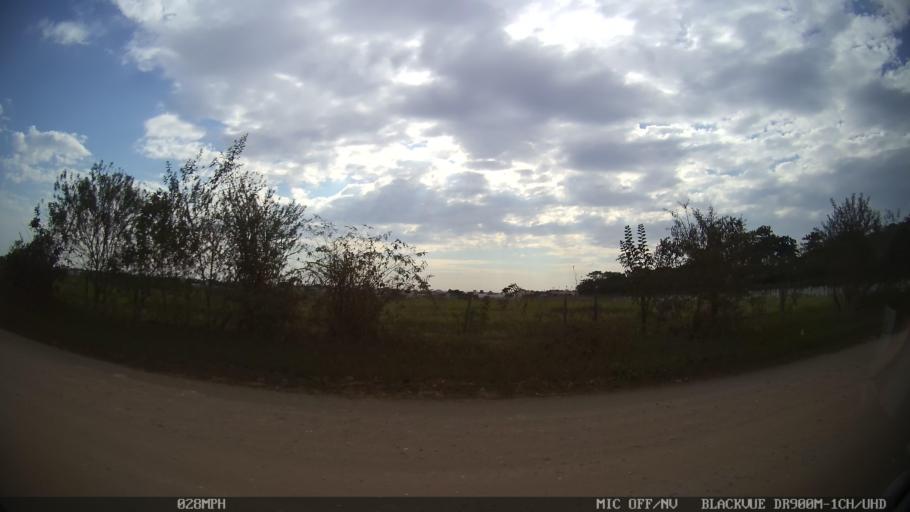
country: BR
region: Sao Paulo
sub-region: Paulinia
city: Paulinia
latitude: -22.7231
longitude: -47.1626
